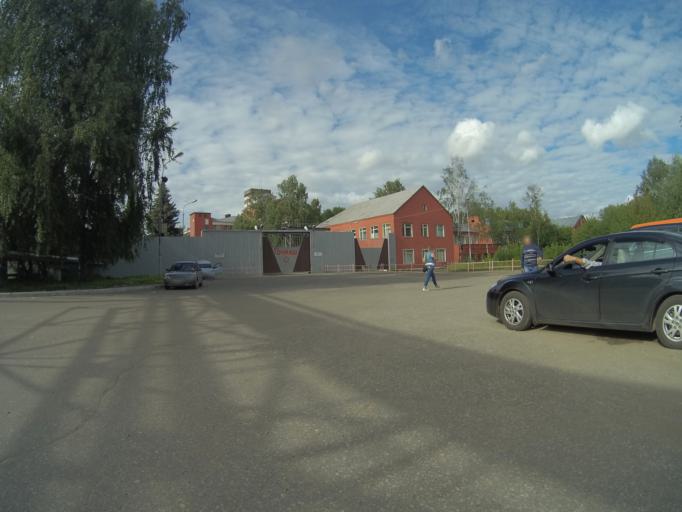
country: RU
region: Vladimir
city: Kommunar
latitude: 56.1504
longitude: 40.4367
